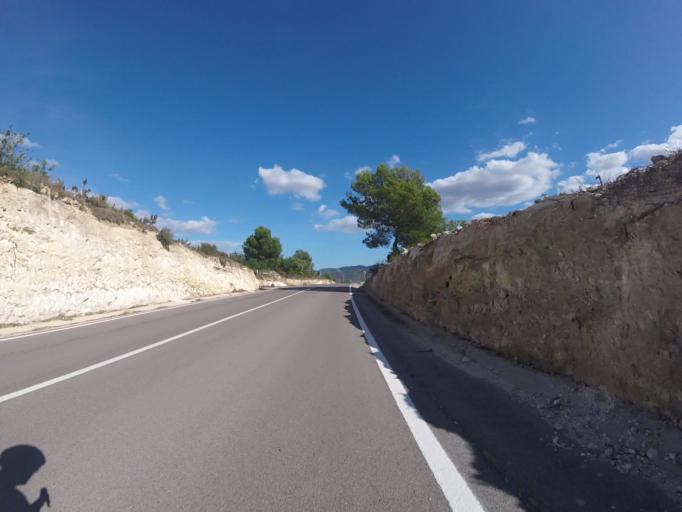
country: ES
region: Valencia
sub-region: Provincia de Castello
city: Alcala de Xivert
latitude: 40.3020
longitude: 0.1910
